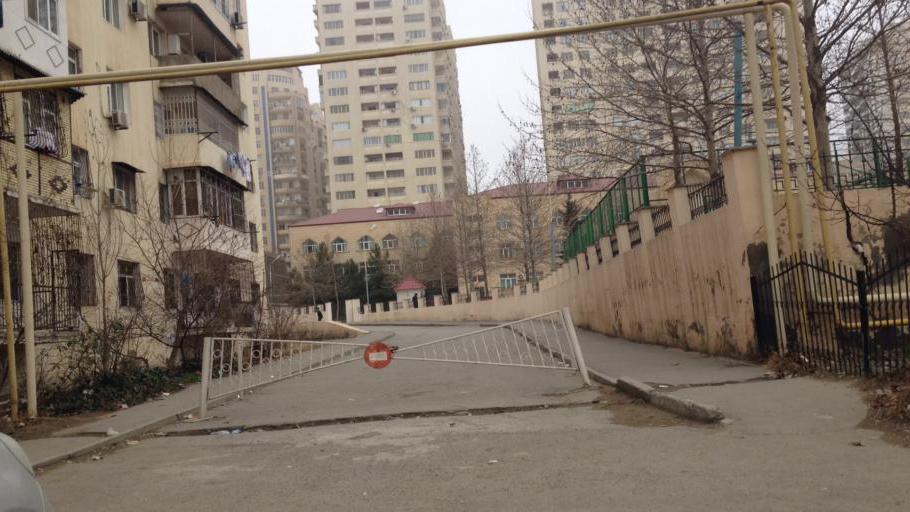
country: AZ
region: Baki
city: Baku
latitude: 40.3869
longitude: 49.8692
